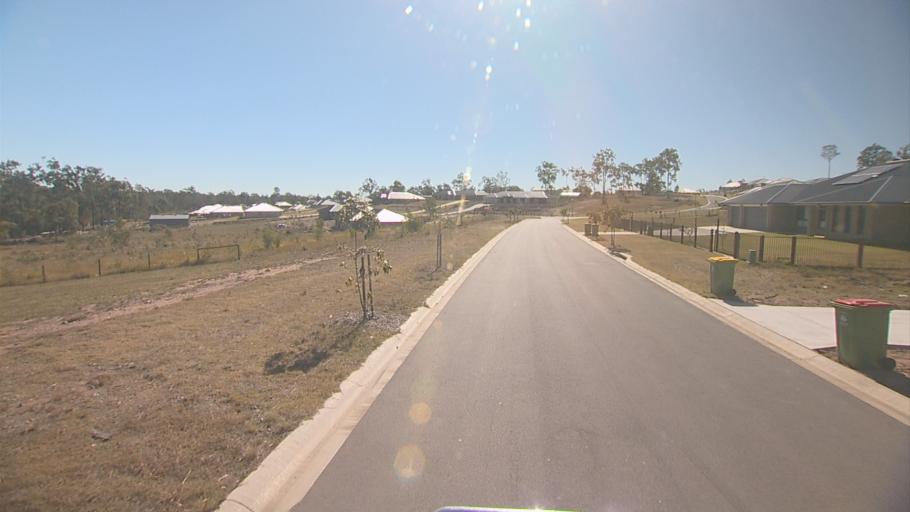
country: AU
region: Queensland
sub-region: Logan
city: North Maclean
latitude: -27.7516
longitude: 152.9438
